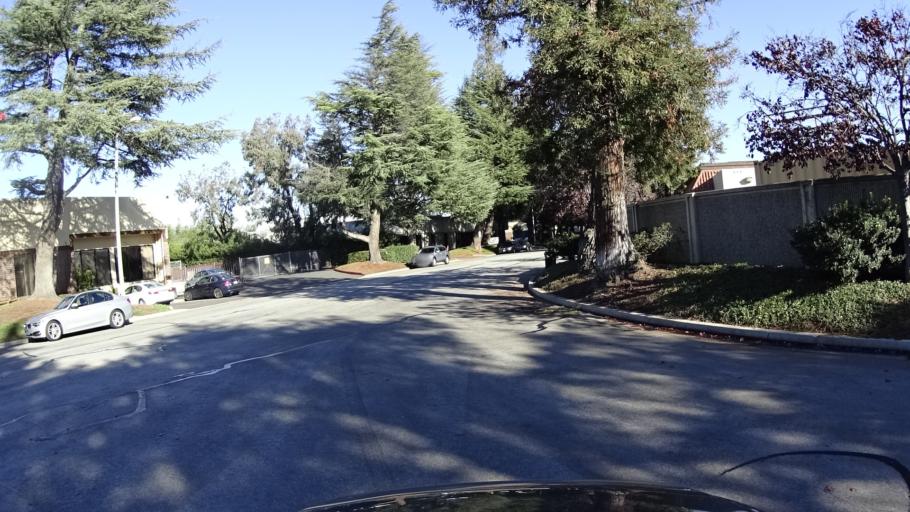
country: US
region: California
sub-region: Santa Clara County
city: Sunnyvale
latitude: 37.3714
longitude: -122.0020
